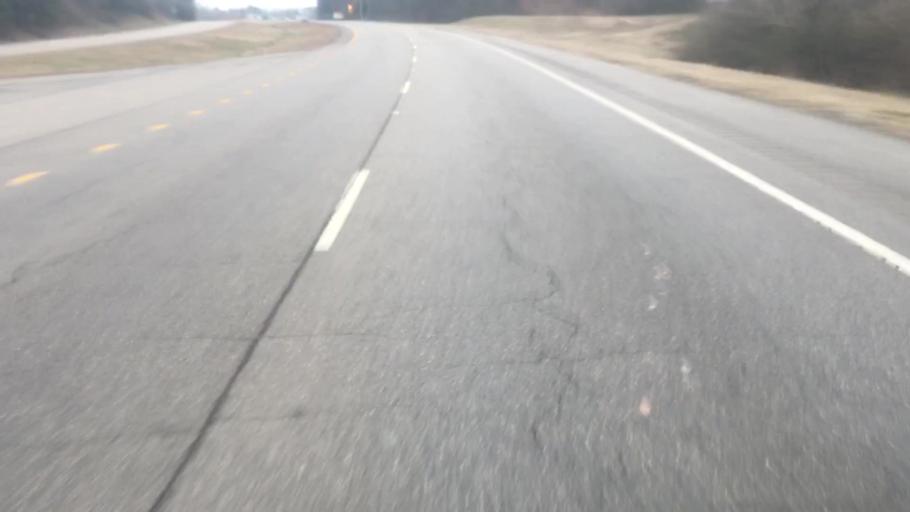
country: US
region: Alabama
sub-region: Walker County
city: Sumiton
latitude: 33.7480
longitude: -87.0554
